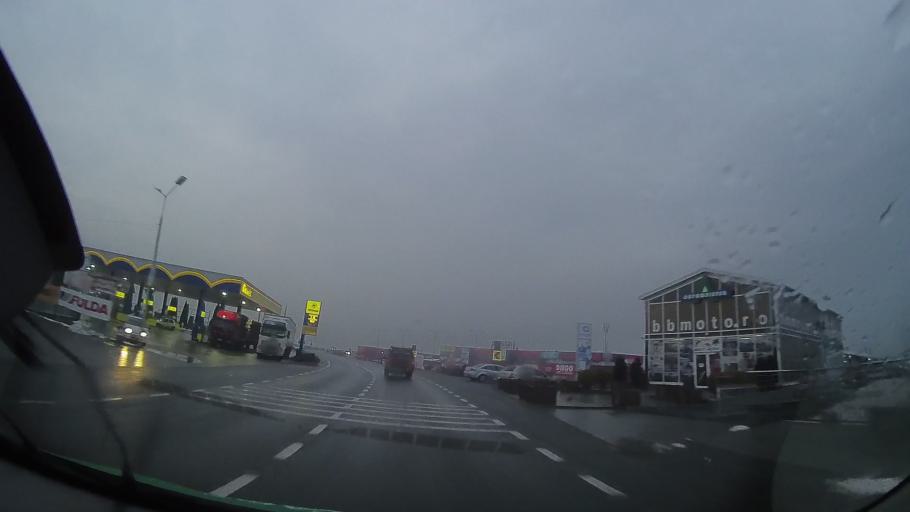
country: RO
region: Harghita
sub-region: Municipiul Gheorgheni
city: Gheorgheni
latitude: 46.7280
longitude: 25.5825
